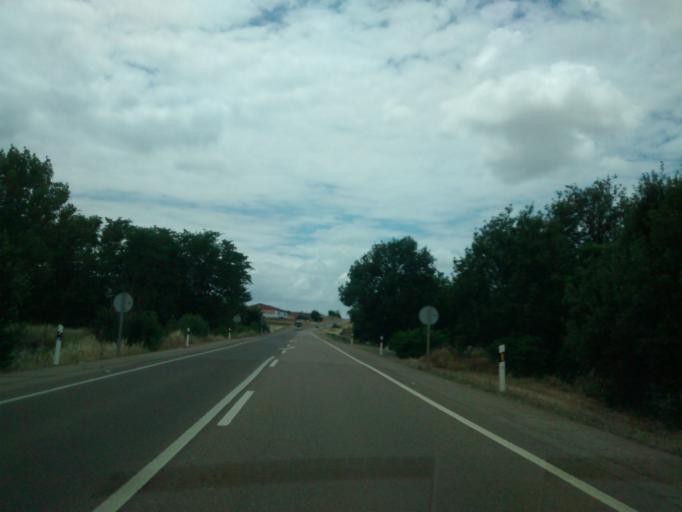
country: ES
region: Extremadura
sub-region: Provincia de Badajoz
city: Merida
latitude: 38.9356
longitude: -6.3059
